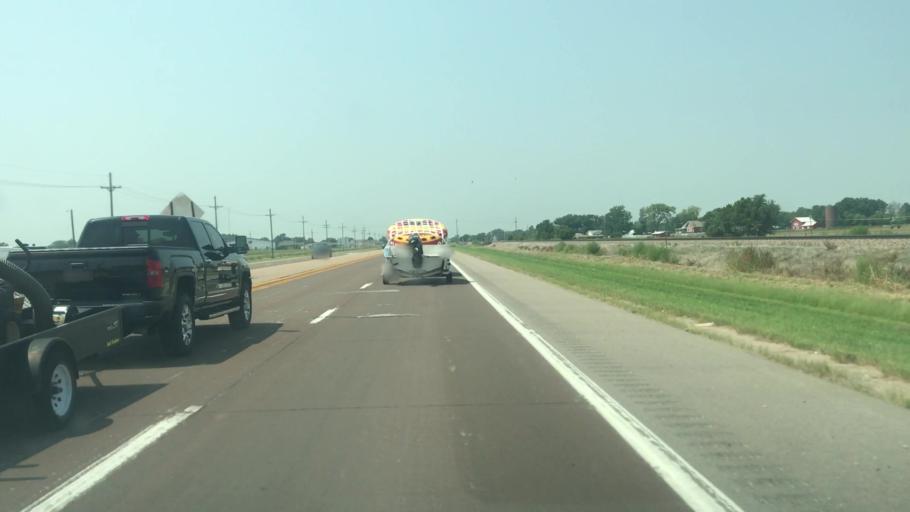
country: US
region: Nebraska
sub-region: Hall County
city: Grand Island
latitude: 40.9554
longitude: -98.3926
